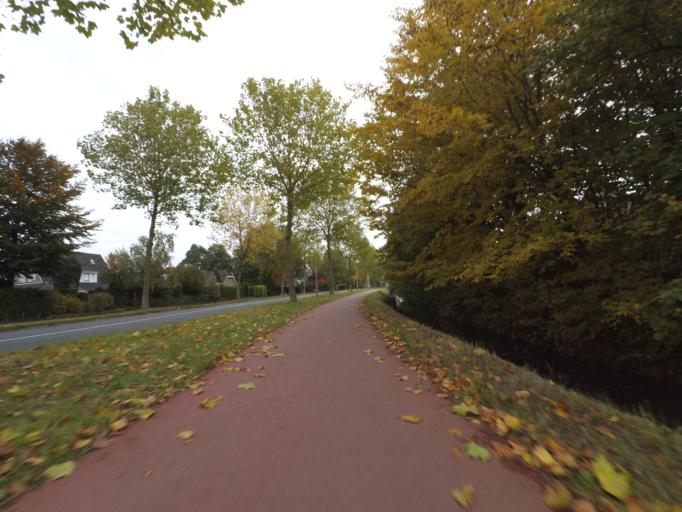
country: NL
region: Gelderland
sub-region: Gemeente Nijkerk
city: Nijkerk
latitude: 52.2184
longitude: 5.4696
